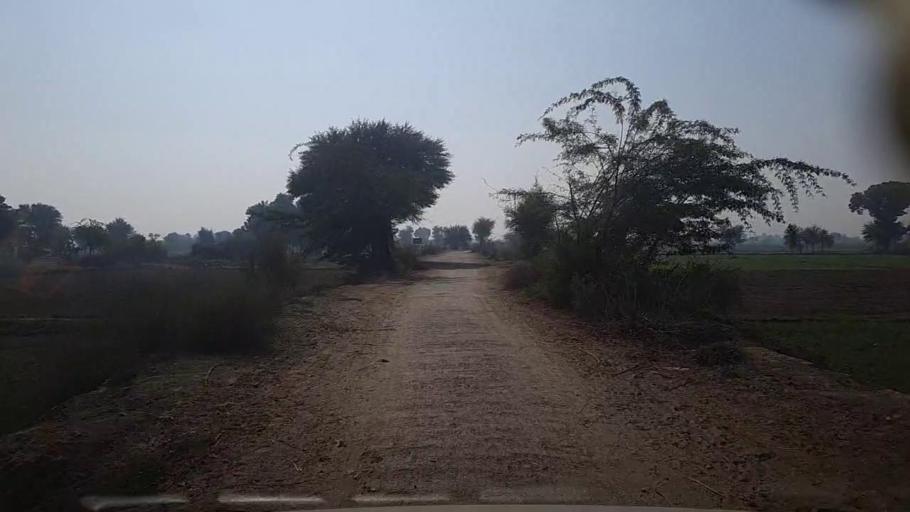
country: PK
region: Sindh
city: Kandiari
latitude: 26.9993
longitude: 68.4916
